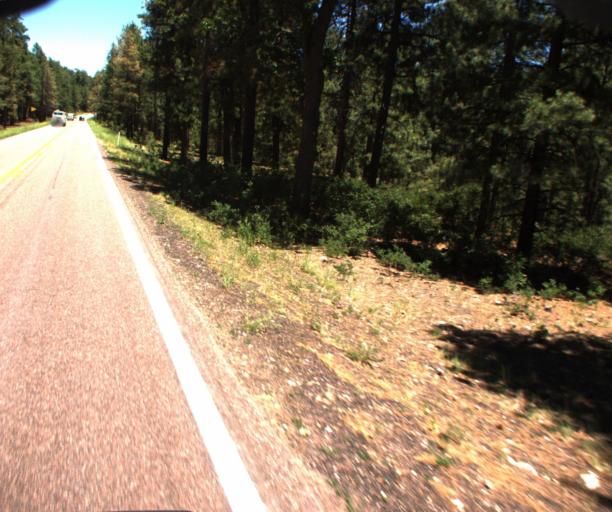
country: US
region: Arizona
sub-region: Gila County
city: Pine
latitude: 34.4476
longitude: -111.4493
